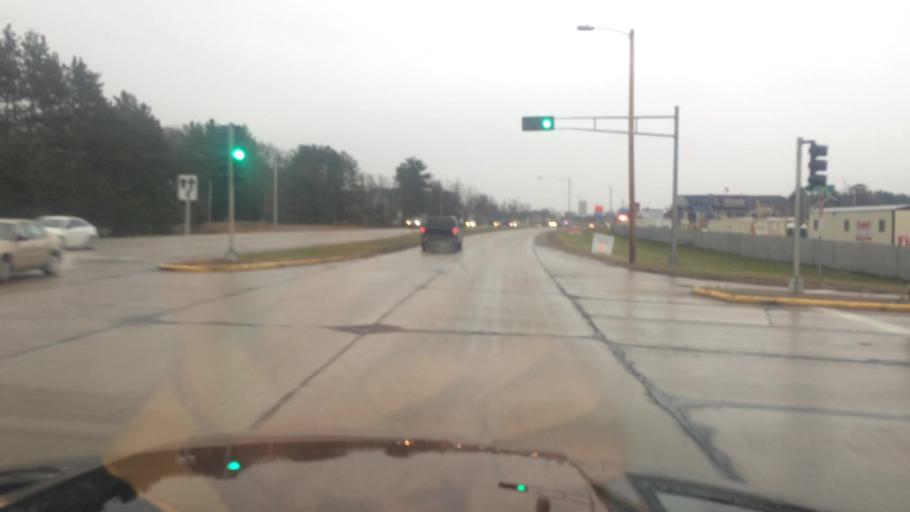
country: US
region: Wisconsin
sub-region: Portage County
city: Stevens Point
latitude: 44.5413
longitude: -89.5759
